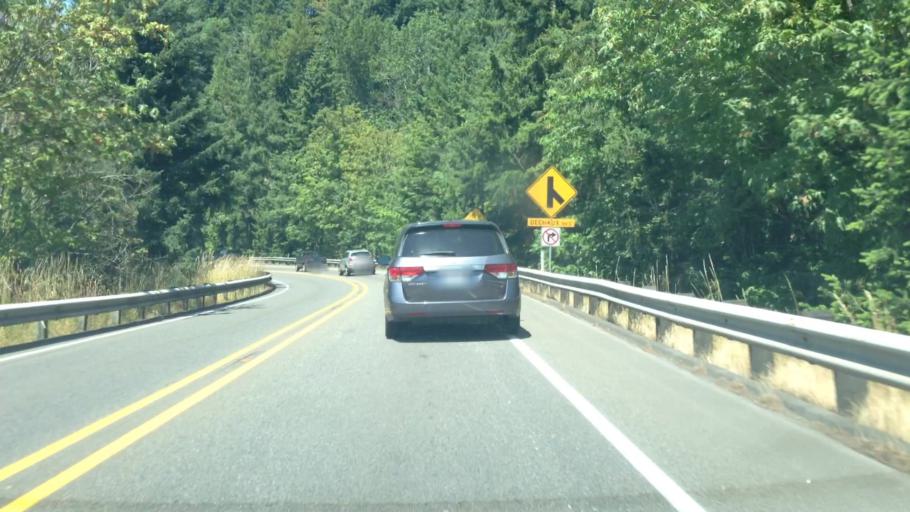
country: US
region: Washington
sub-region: Pierce County
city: North Puyallup
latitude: 47.2143
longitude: -122.2939
